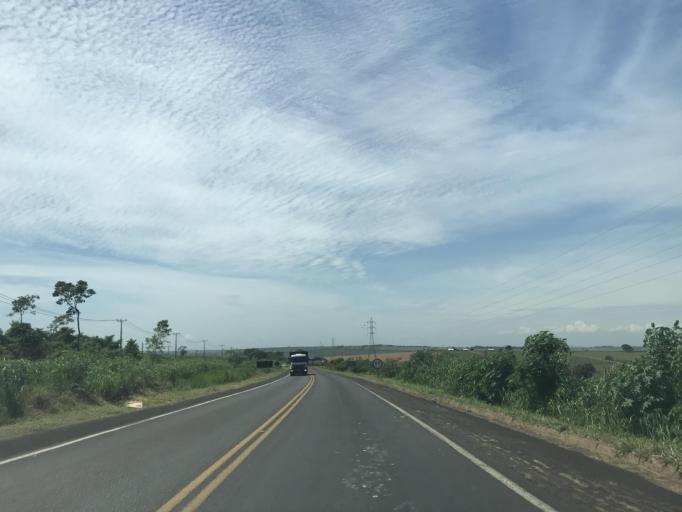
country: BR
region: Parana
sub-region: Paranavai
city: Nova Aurora
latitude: -22.9892
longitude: -52.5974
